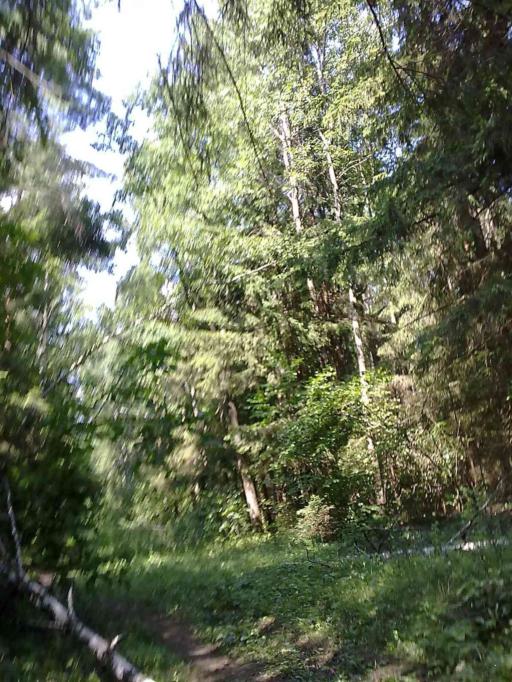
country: RU
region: Moskovskaya
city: Kokoshkino
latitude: 55.6119
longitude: 37.1769
